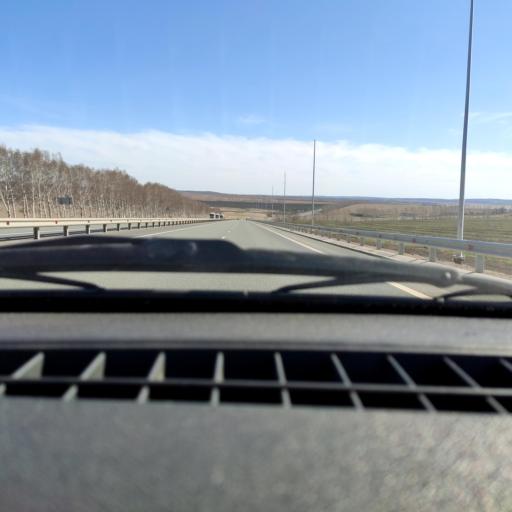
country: RU
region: Bashkortostan
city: Karmaskaly
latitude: 54.3663
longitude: 55.9170
